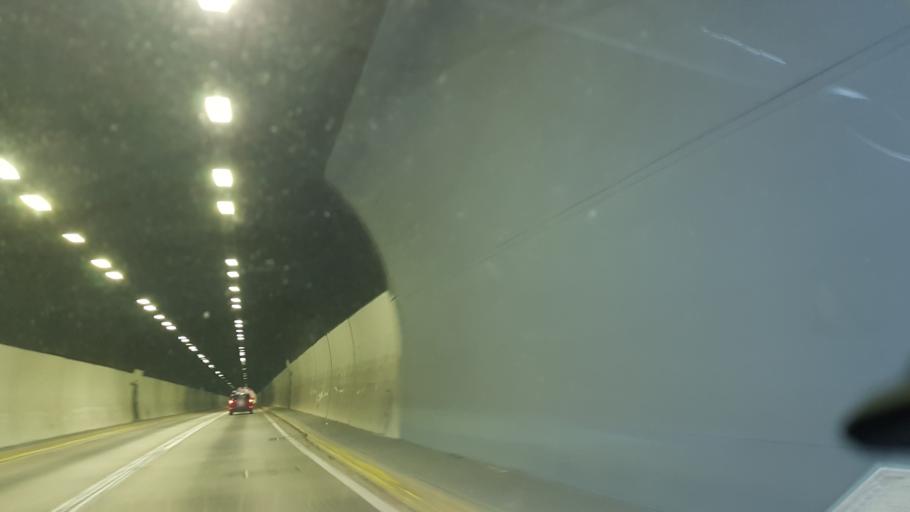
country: CL
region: Valparaiso
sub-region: Provincia de Valparaiso
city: Valparaiso
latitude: -33.0390
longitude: -71.6530
